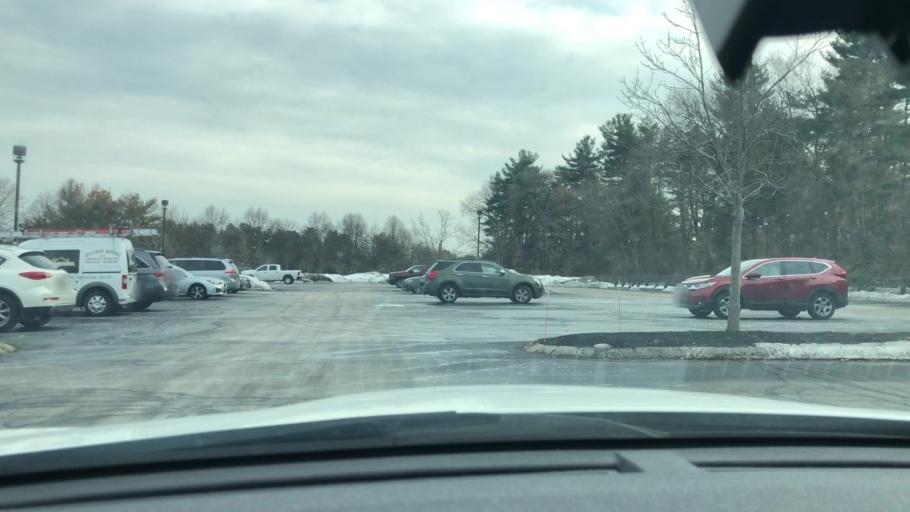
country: US
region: Massachusetts
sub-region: Middlesex County
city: Lowell
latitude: 42.6015
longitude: -71.3284
